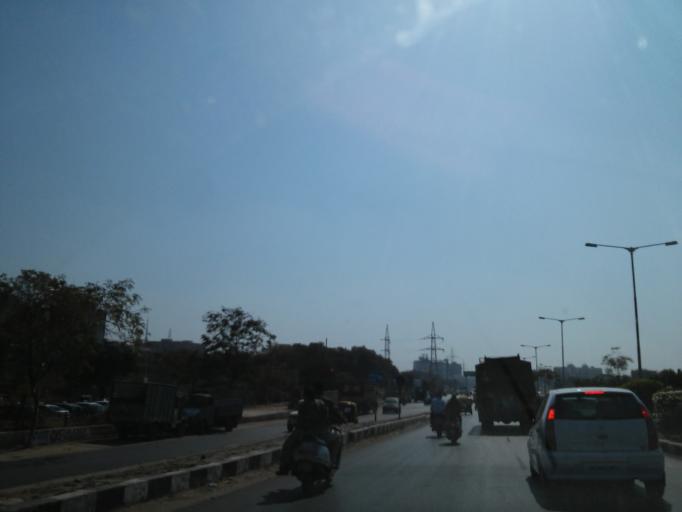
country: IN
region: Gujarat
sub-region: Ahmadabad
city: Ahmedabad
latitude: 23.0622
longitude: 72.5212
